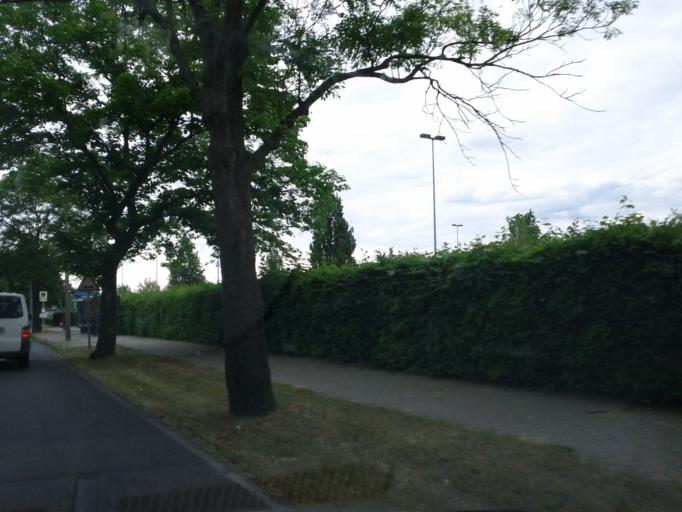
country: DE
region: Berlin
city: Hellersdorf
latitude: 52.5474
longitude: 13.6001
